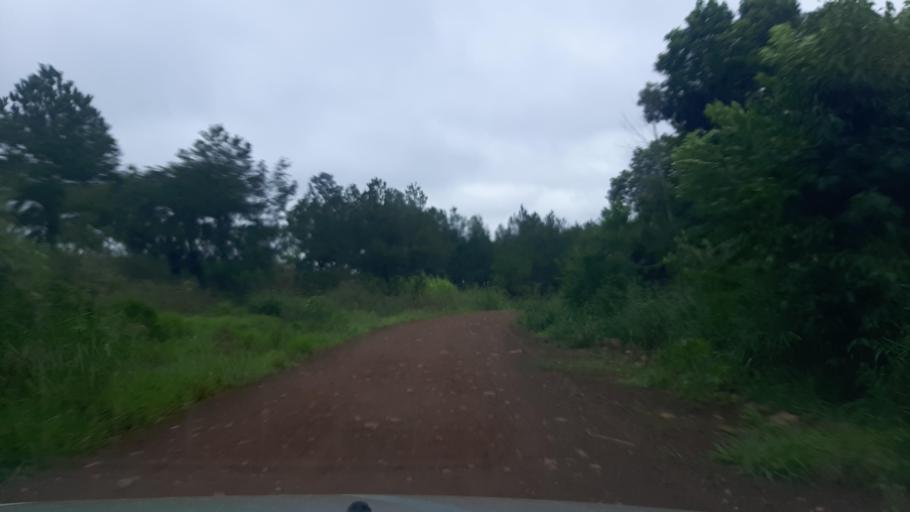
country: BR
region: Parana
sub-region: Ampere
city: Ampere
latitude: -26.0514
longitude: -53.5548
